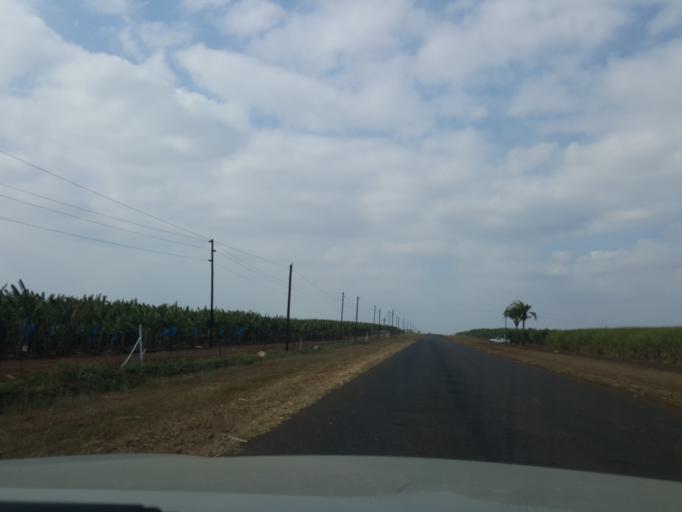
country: ZA
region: Mpumalanga
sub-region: Ehlanzeni District
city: Komatipoort
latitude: -25.3906
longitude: 31.9008
